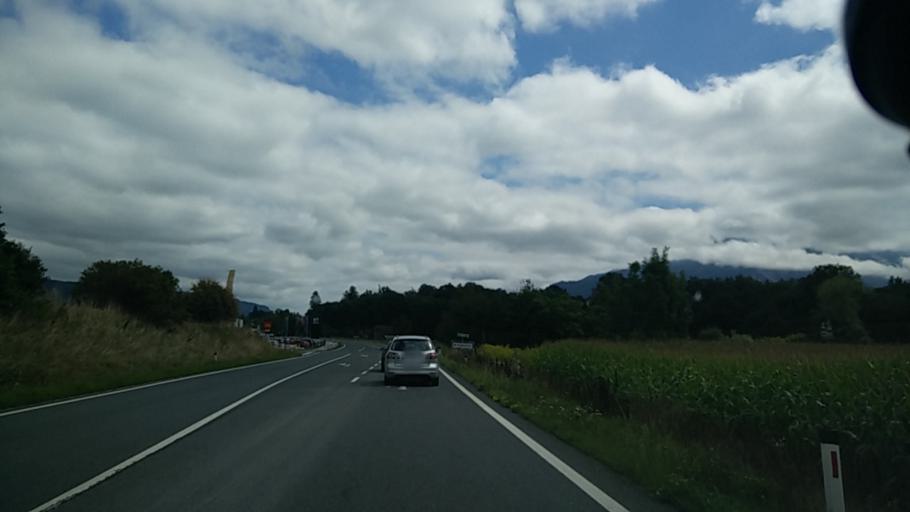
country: AT
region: Carinthia
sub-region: Politischer Bezirk Klagenfurt Land
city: Ferlach
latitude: 46.5320
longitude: 14.2686
